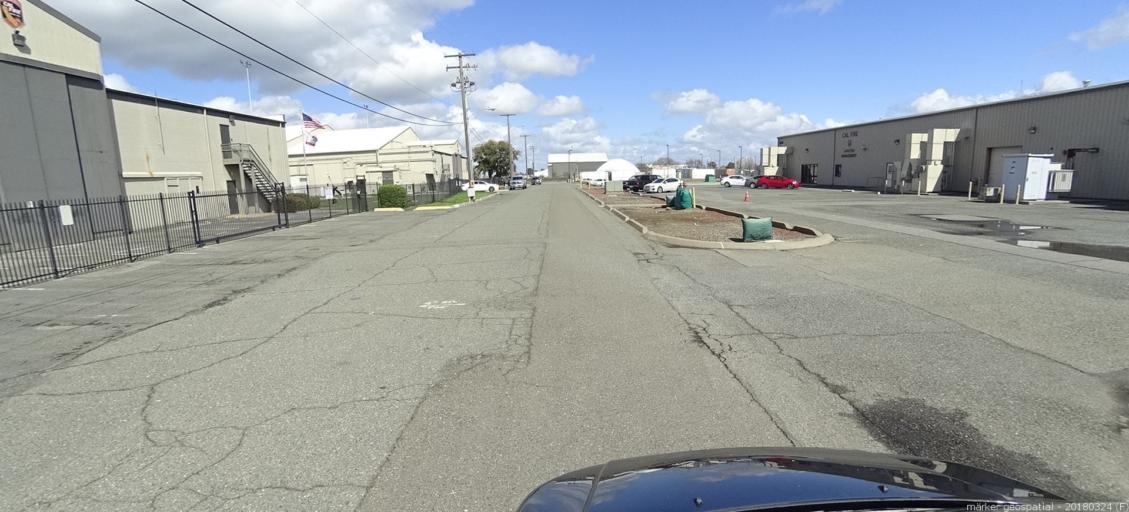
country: US
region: California
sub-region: Sacramento County
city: North Highlands
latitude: 38.6662
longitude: -121.3933
